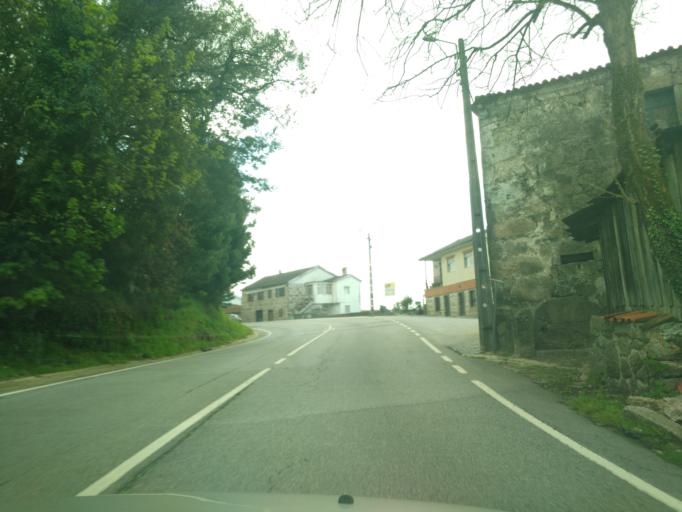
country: PT
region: Braga
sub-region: Braga
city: Braga
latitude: 41.5054
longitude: -8.4166
